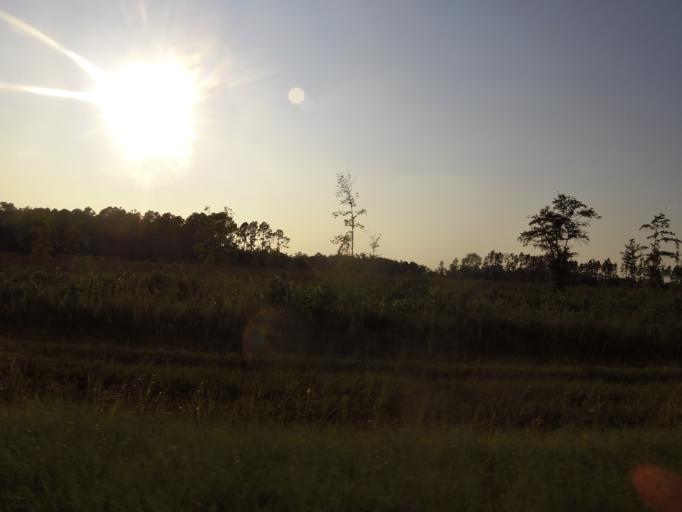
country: US
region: Florida
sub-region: Nassau County
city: Callahan
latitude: 30.5256
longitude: -81.9924
